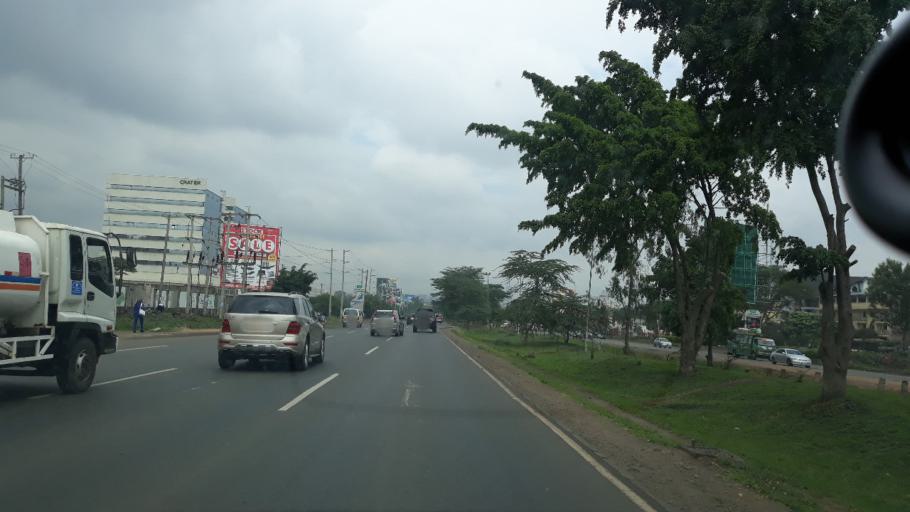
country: KE
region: Nairobi Area
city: Pumwani
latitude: -1.3232
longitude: 36.8440
